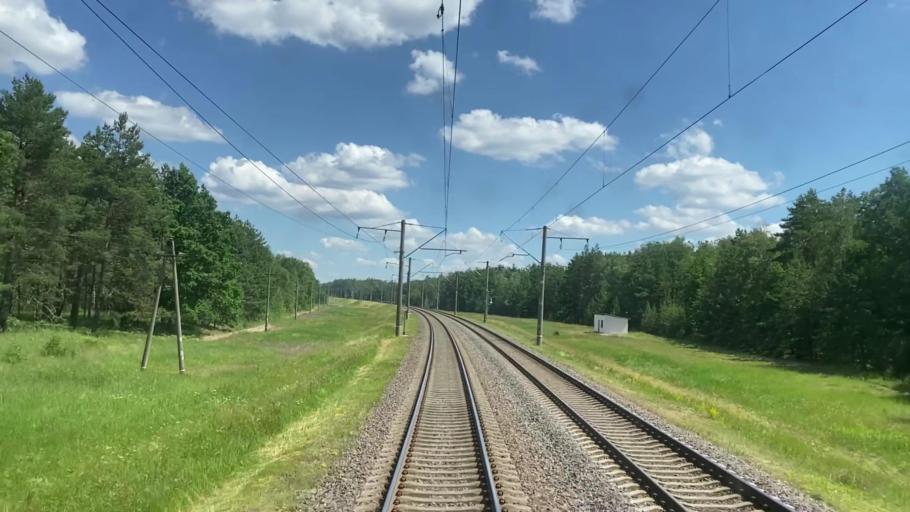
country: BY
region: Brest
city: Ivatsevichy
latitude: 52.8440
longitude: 25.5568
